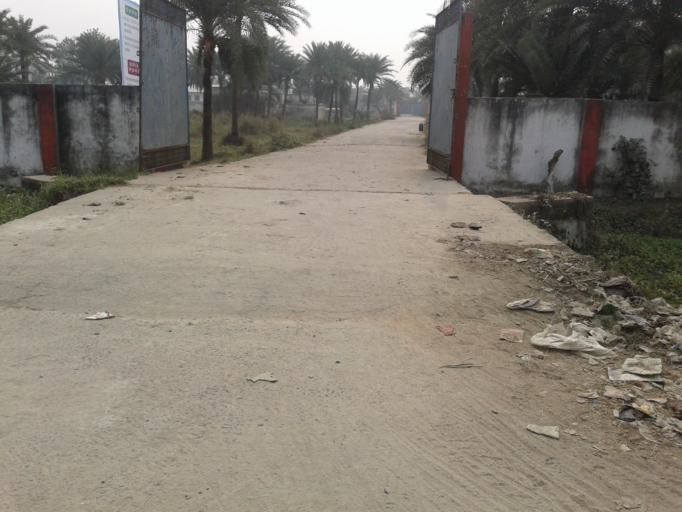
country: IN
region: Bihar
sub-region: Muzaffarpur
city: Muzaffarpur
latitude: 26.1023
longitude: 85.4059
